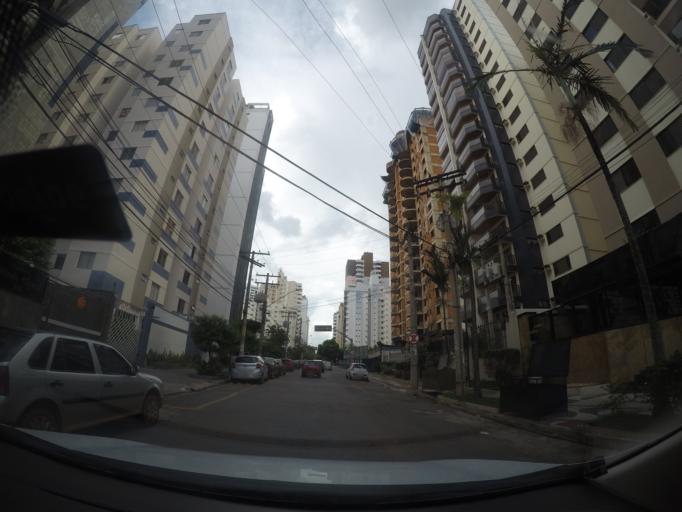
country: BR
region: Goias
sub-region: Goiania
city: Goiania
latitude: -16.7149
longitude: -49.2692
